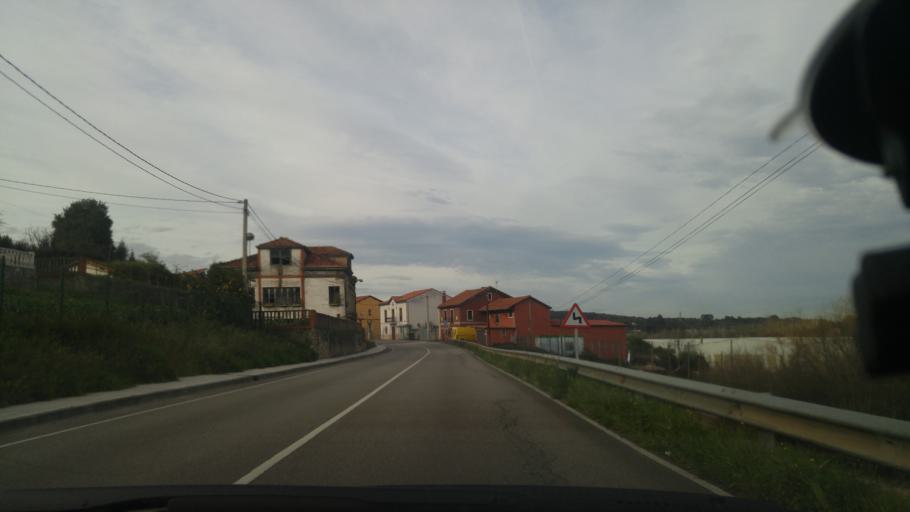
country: ES
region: Asturias
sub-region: Province of Asturias
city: Corvera de Asturias
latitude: 43.5209
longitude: -5.8706
